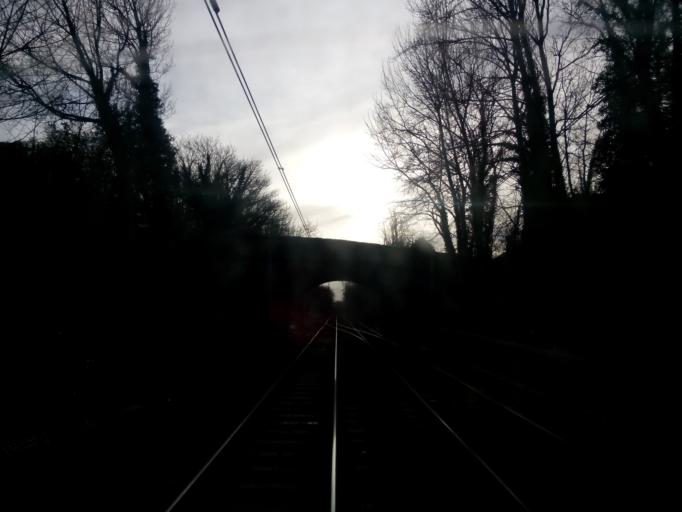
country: GB
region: England
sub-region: Newcastle upon Tyne
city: Gosforth
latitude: 55.0046
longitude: -1.6088
